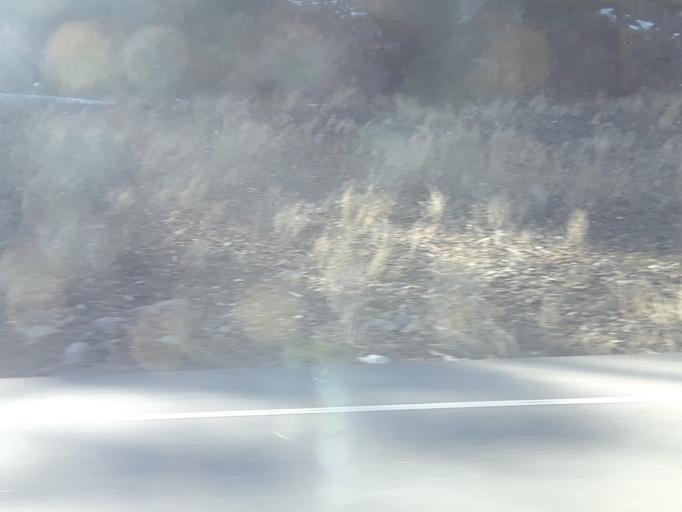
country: US
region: Colorado
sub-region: Boulder County
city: Boulder
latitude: 40.1075
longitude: -105.3195
